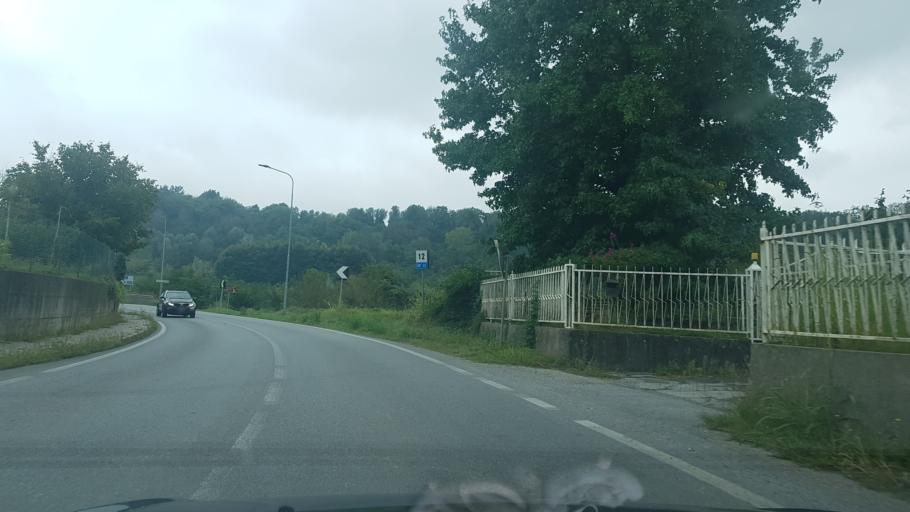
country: IT
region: Piedmont
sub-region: Provincia di Cuneo
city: Bastia Mondovi
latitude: 44.4426
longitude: 7.8915
